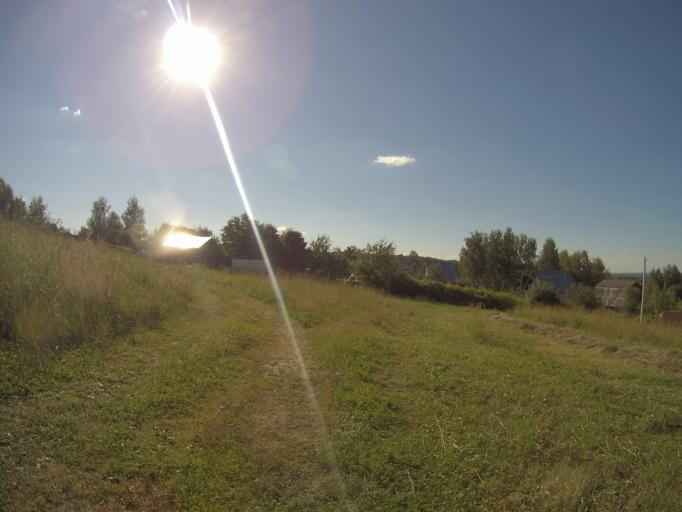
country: RU
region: Vladimir
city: Raduzhnyy
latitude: 55.9990
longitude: 40.3688
